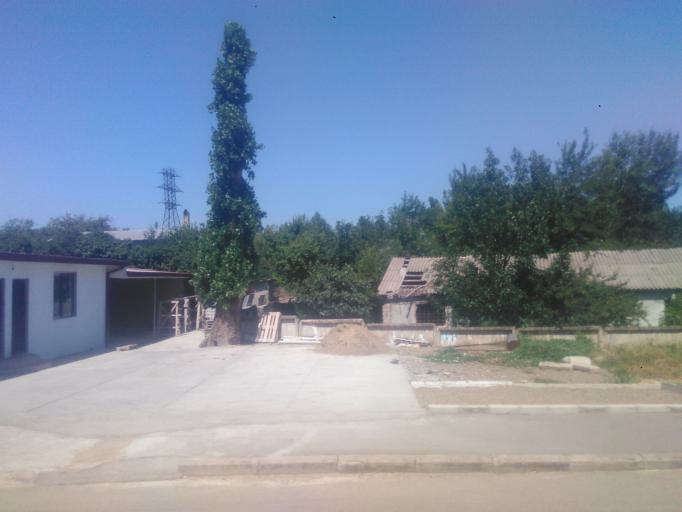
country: GE
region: T'bilisi
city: Tbilisi
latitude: 41.7058
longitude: 44.8872
